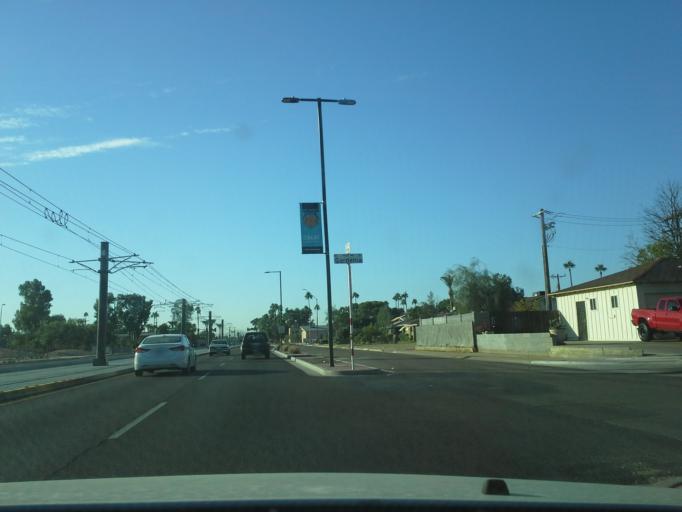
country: US
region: Arizona
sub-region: Maricopa County
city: Glendale
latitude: 33.5446
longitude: -112.0997
